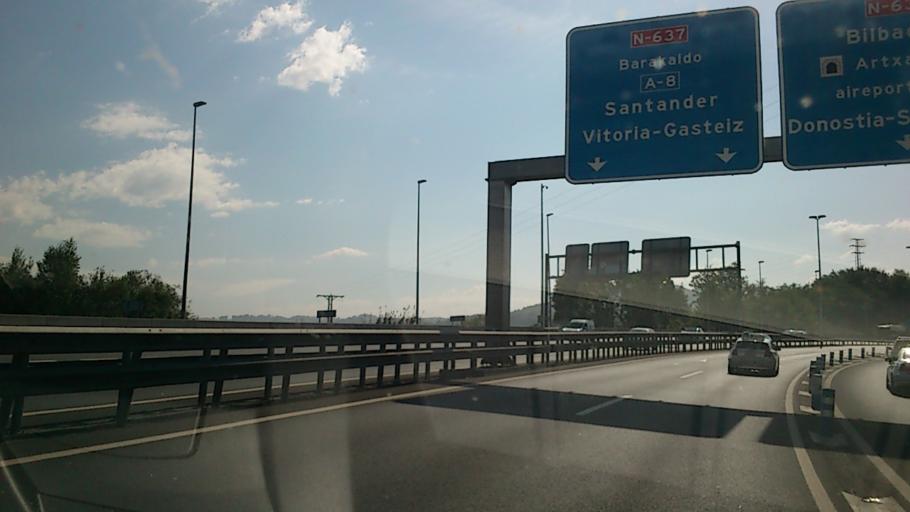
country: ES
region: Basque Country
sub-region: Bizkaia
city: Erandio
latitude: 43.3059
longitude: -2.9615
